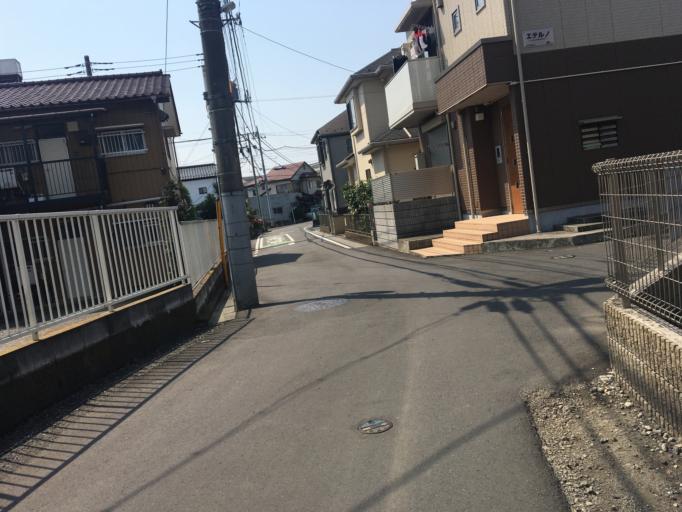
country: JP
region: Saitama
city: Kawagoe
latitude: 35.9226
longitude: 139.4435
